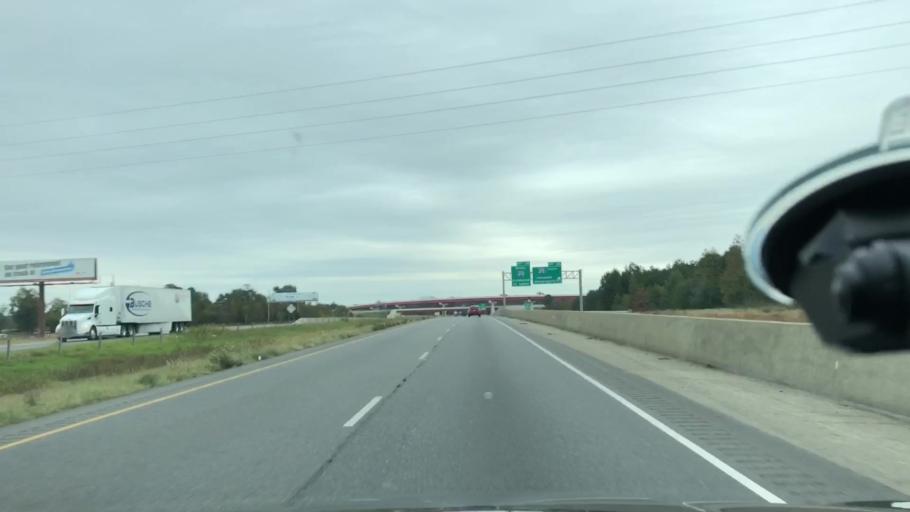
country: US
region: Arkansas
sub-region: Miller County
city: Texarkana
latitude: 33.4782
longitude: -93.9943
